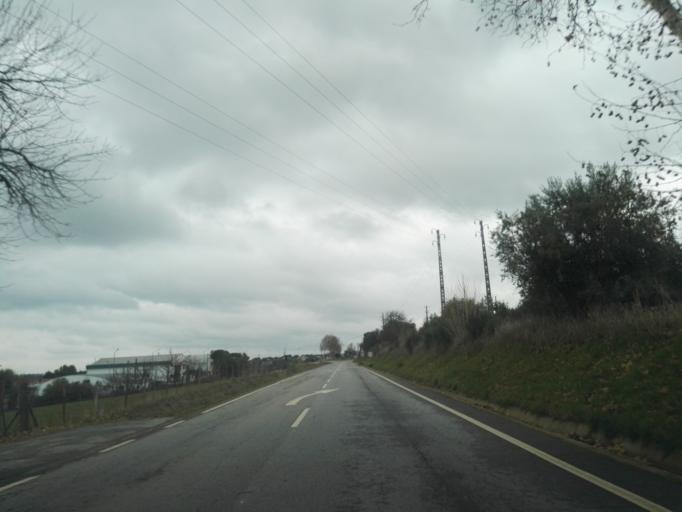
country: PT
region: Portalegre
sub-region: Arronches
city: Arronches
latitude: 39.1167
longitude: -7.2905
